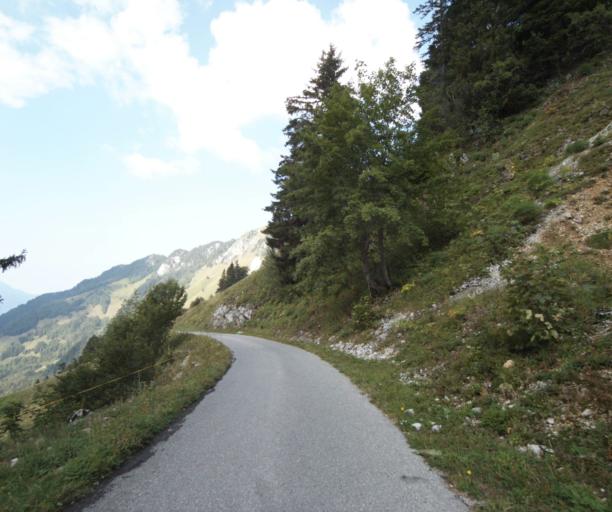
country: CH
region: Vaud
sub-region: Riviera-Pays-d'Enhaut District
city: Caux
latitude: 46.4217
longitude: 6.9933
